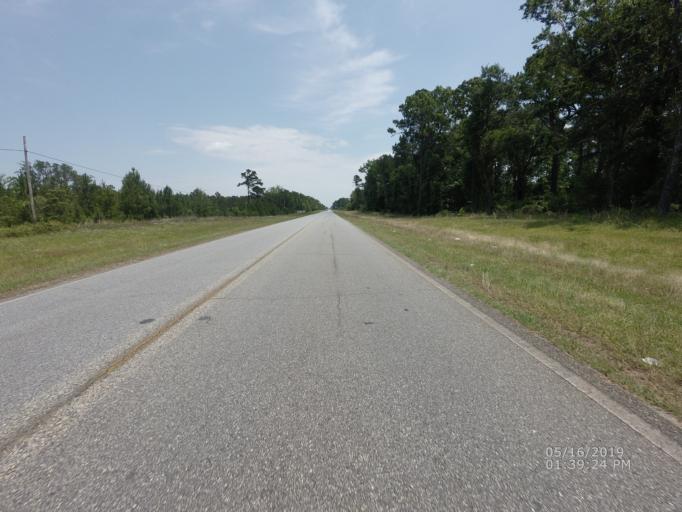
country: US
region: Georgia
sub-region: Dougherty County
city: Albany
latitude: 31.5490
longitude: -84.2432
